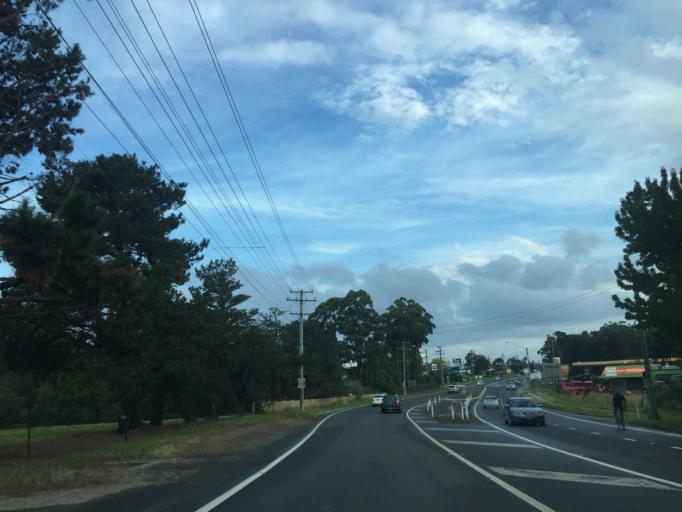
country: AU
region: New South Wales
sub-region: The Hills Shire
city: Glenhaven
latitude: -33.6926
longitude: 151.0324
